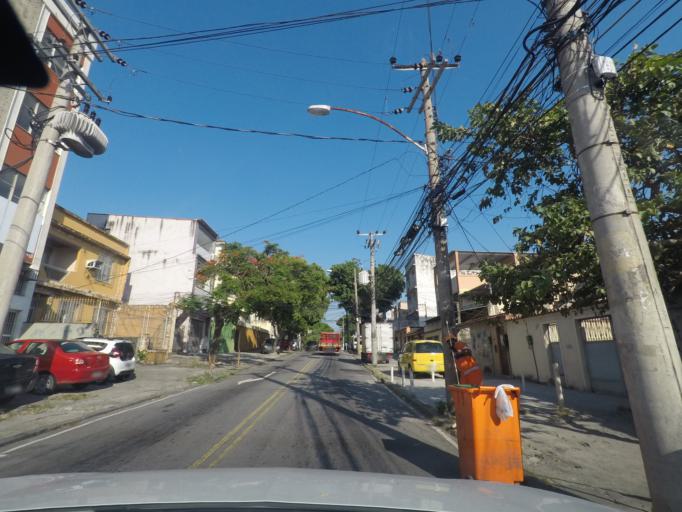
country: BR
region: Rio de Janeiro
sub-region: Duque De Caxias
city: Duque de Caxias
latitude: -22.8323
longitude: -43.2799
